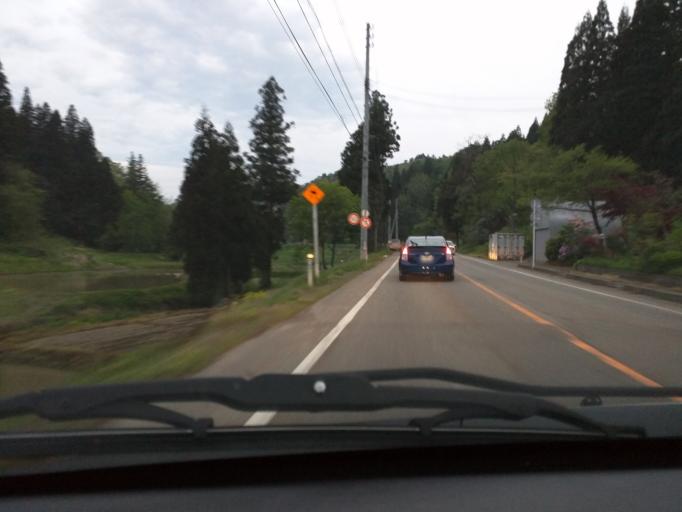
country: JP
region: Niigata
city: Ojiya
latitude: 37.3195
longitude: 138.6979
